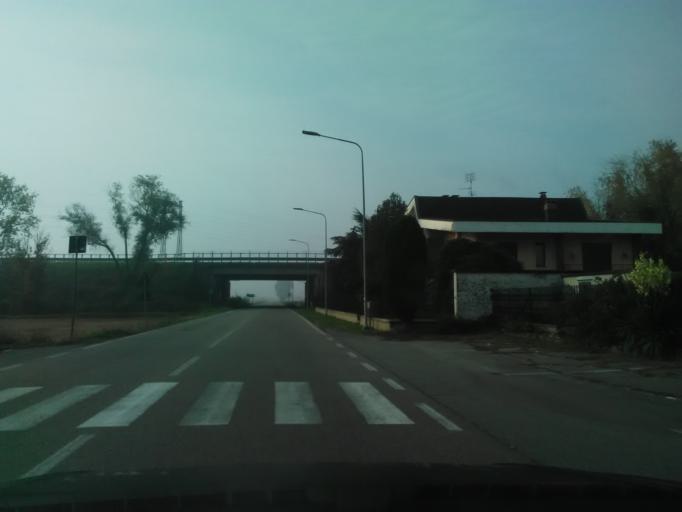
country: IT
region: Piedmont
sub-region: Provincia di Vercelli
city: Santhia
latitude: 45.3558
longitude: 8.1715
